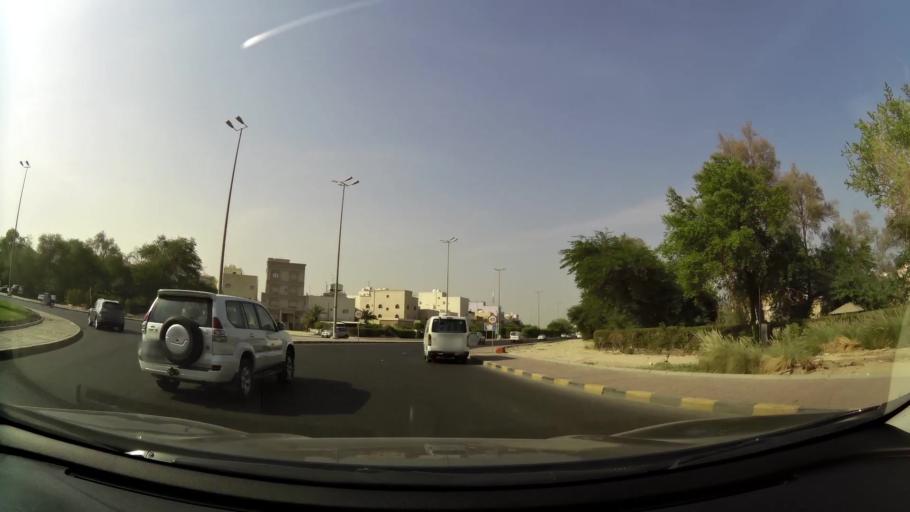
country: KW
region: Mubarak al Kabir
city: Mubarak al Kabir
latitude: 29.1753
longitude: 48.0846
